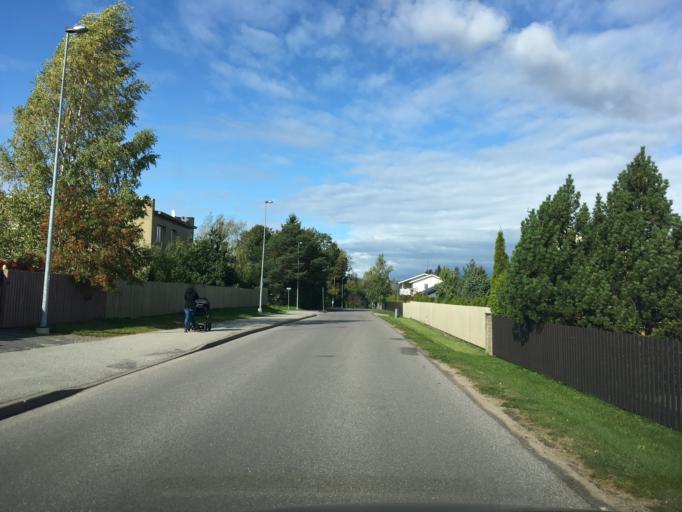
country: EE
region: Harju
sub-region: Saue vald
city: Laagri
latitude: 59.3486
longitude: 24.6394
